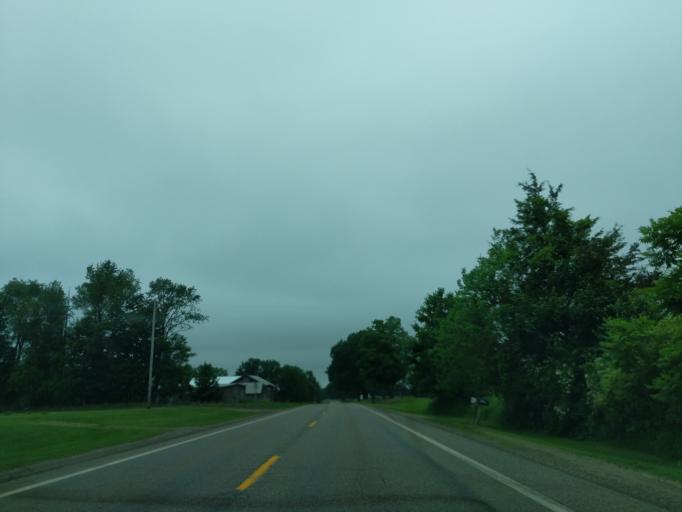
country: US
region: Michigan
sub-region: Hillsdale County
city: Litchfield
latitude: 42.0840
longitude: -84.8029
